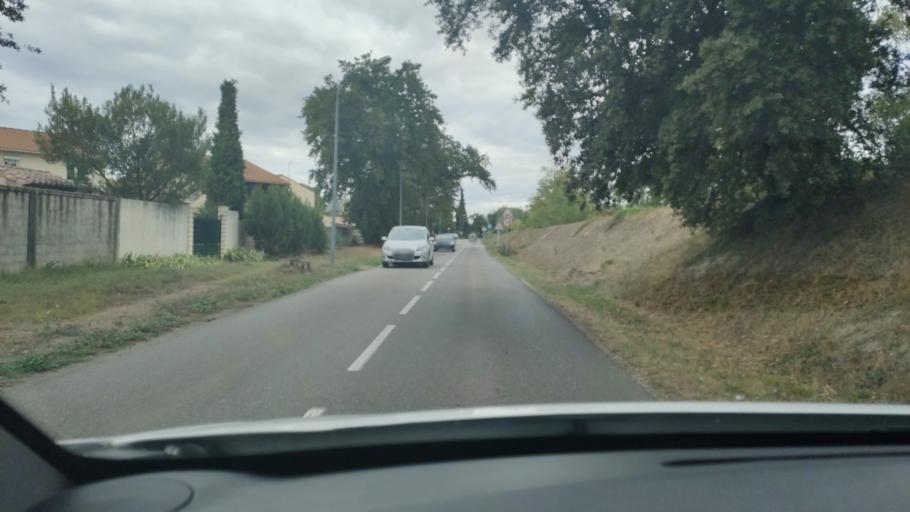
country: FR
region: Provence-Alpes-Cote d'Azur
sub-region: Departement du Vaucluse
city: Le Pontet
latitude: 43.9626
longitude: 4.8829
